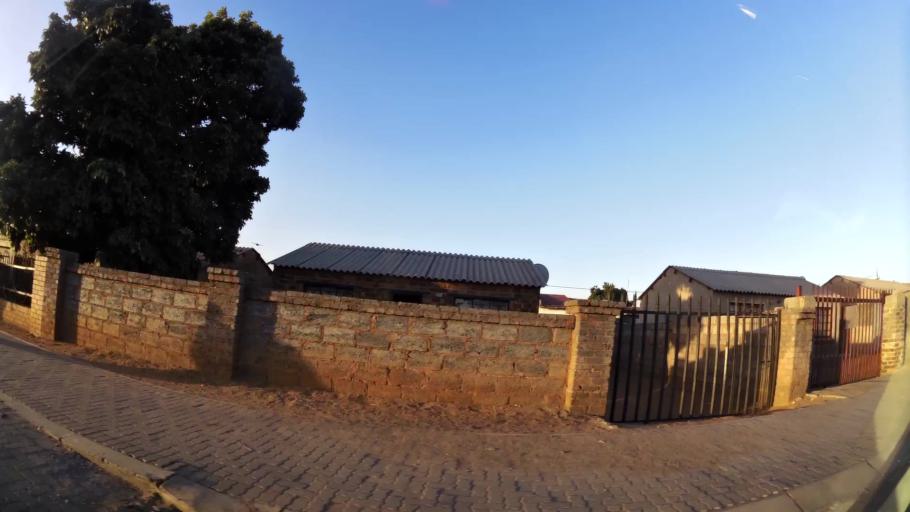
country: ZA
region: Gauteng
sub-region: Ekurhuleni Metropolitan Municipality
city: Tembisa
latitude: -25.9991
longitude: 28.2210
